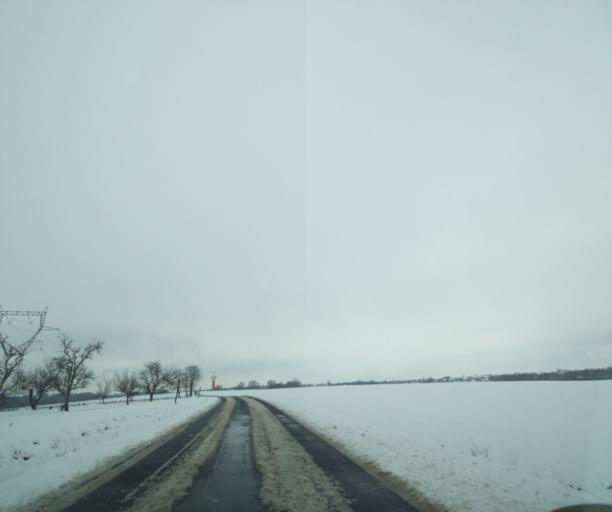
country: FR
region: Champagne-Ardenne
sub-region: Departement de la Haute-Marne
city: Montier-en-Der
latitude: 48.5087
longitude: 4.7163
